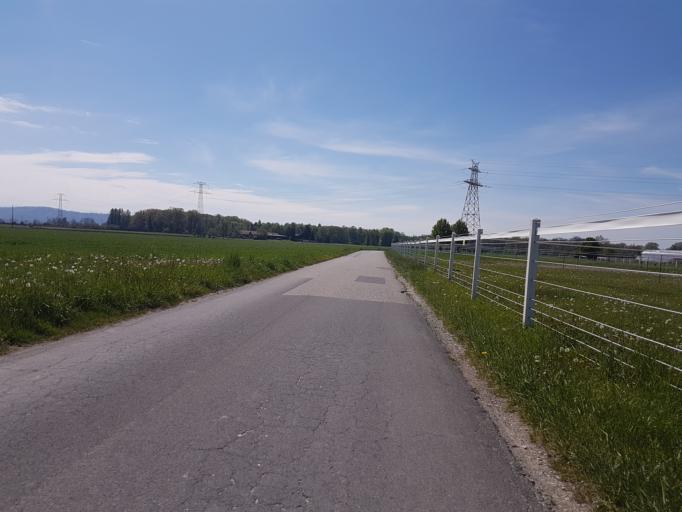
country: CH
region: Neuchatel
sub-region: Neuchatel District
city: Cornaux
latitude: 47.0179
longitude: 7.0364
